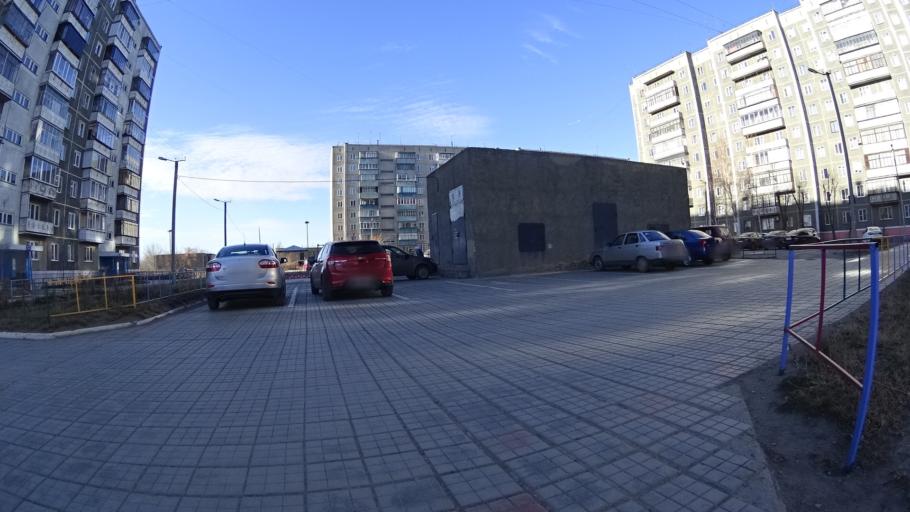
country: RU
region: Chelyabinsk
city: Troitsk
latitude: 54.0466
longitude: 61.6427
